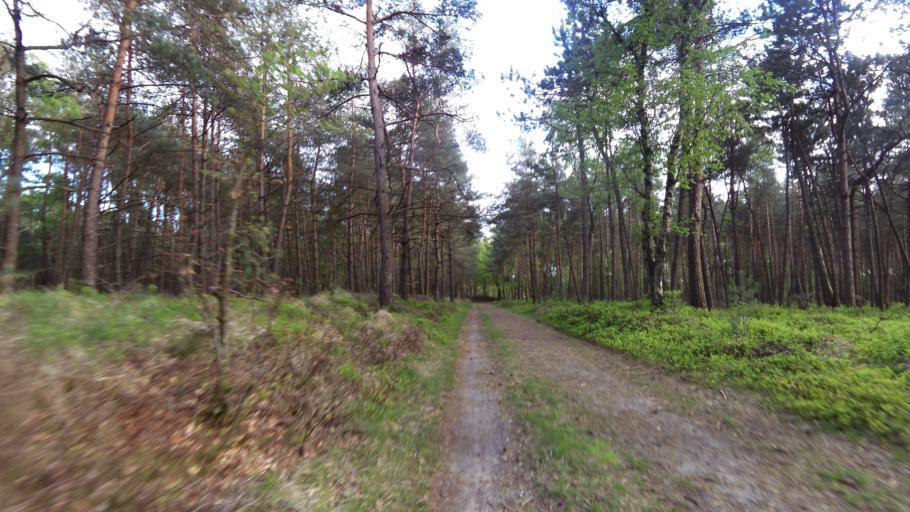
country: NL
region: Gelderland
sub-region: Gemeente Rozendaal
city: Rozendaal
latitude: 52.0282
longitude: 5.9392
